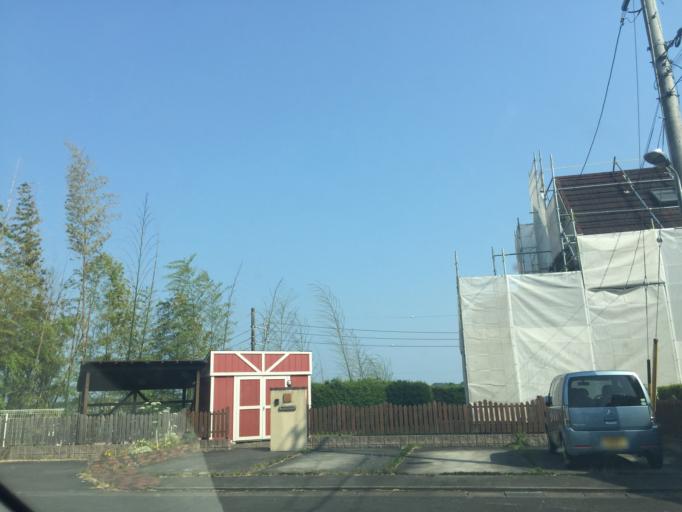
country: JP
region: Shizuoka
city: Kakegawa
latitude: 34.7814
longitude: 137.9947
